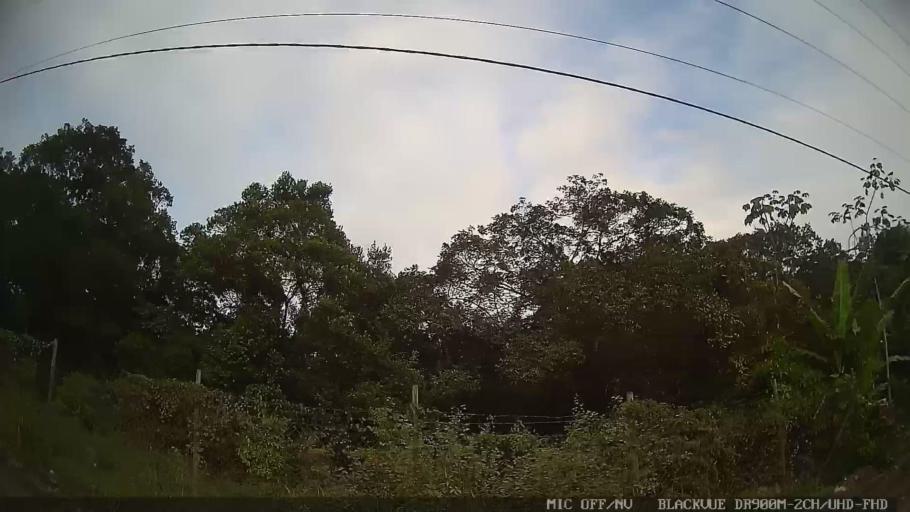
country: BR
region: Sao Paulo
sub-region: Guaruja
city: Guaruja
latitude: -23.9708
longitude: -46.2157
